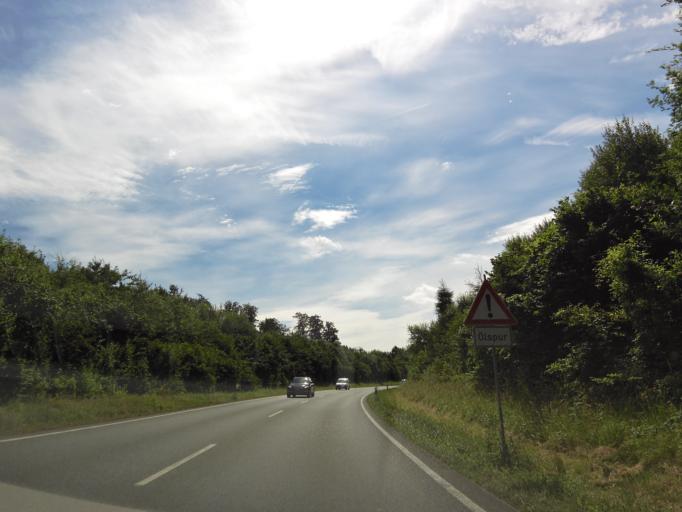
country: DE
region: Lower Saxony
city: Furstenberg
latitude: 51.7056
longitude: 9.3822
